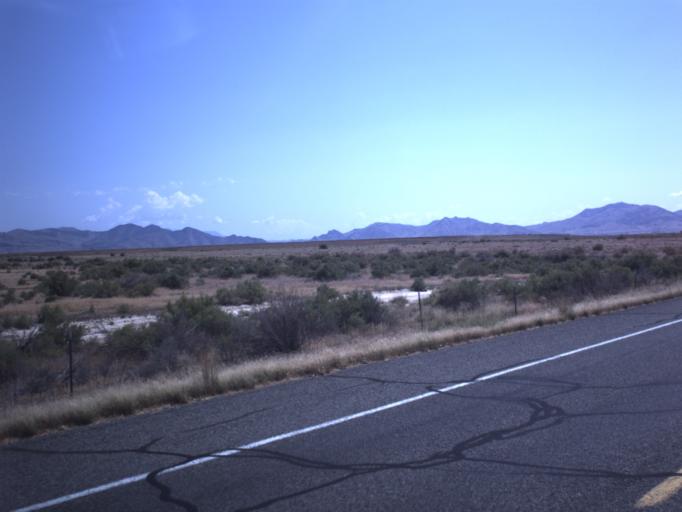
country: US
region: Utah
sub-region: Millard County
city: Delta
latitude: 39.4691
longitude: -112.4552
